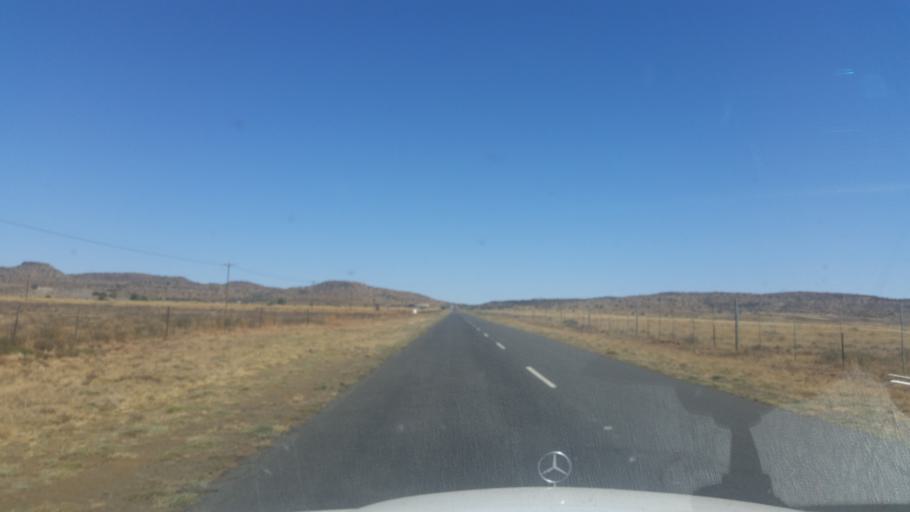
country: ZA
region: Eastern Cape
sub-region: Joe Gqabi District Municipality
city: Burgersdorp
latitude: -30.7825
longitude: 25.7724
